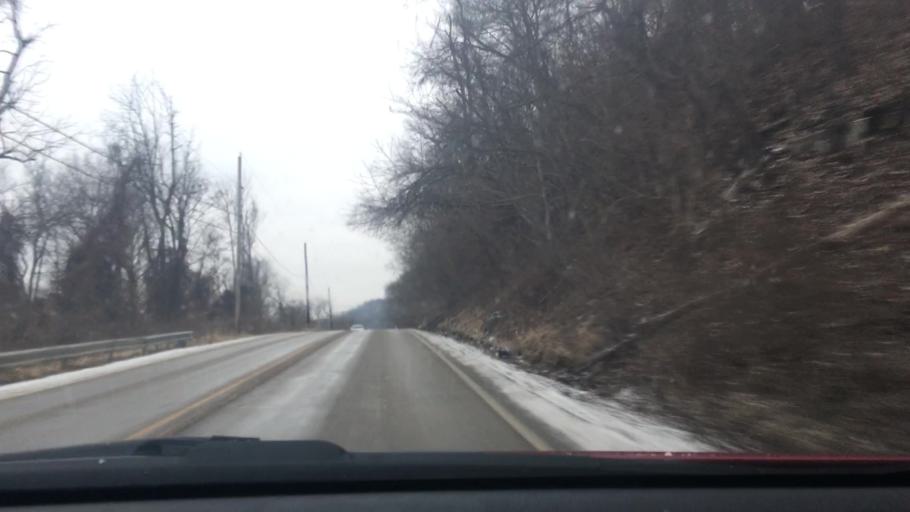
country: US
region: Pennsylvania
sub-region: Washington County
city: New Eagle
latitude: 40.2444
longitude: -79.9431
